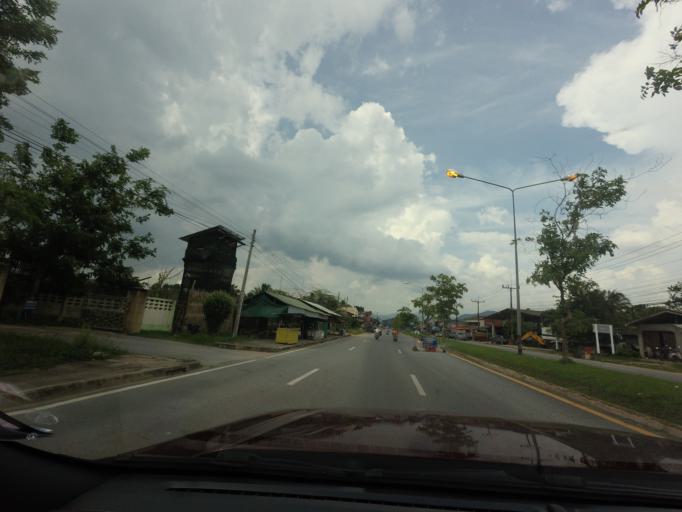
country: TH
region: Yala
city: Ban Nang Sata
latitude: 6.2610
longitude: 101.2559
